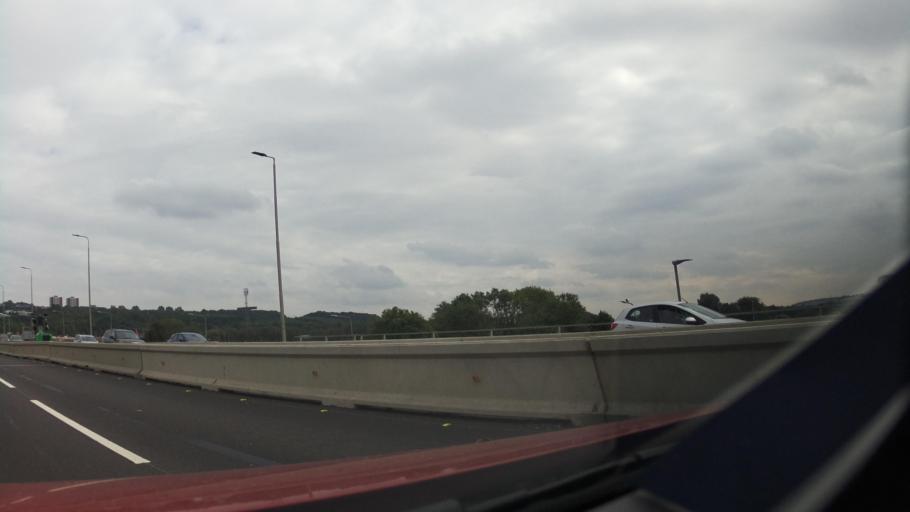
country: GB
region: England
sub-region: Gateshead
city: Lamesley
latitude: 54.9204
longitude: -1.6118
